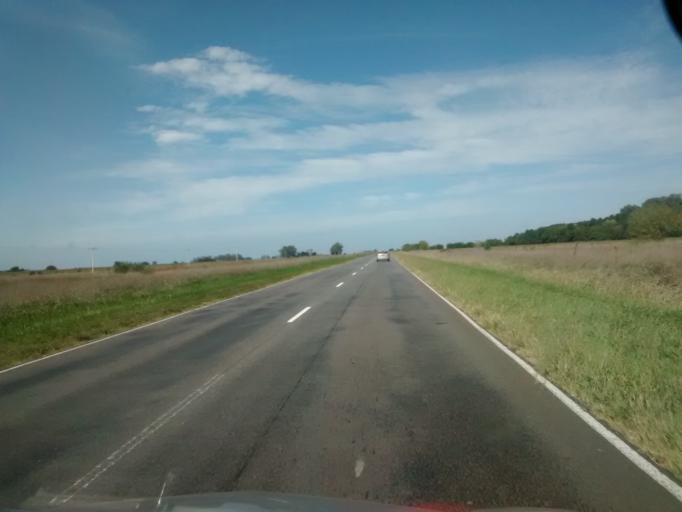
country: AR
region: Buenos Aires
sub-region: Partido de Ayacucho
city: Ayacucho
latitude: -36.6514
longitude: -58.5738
